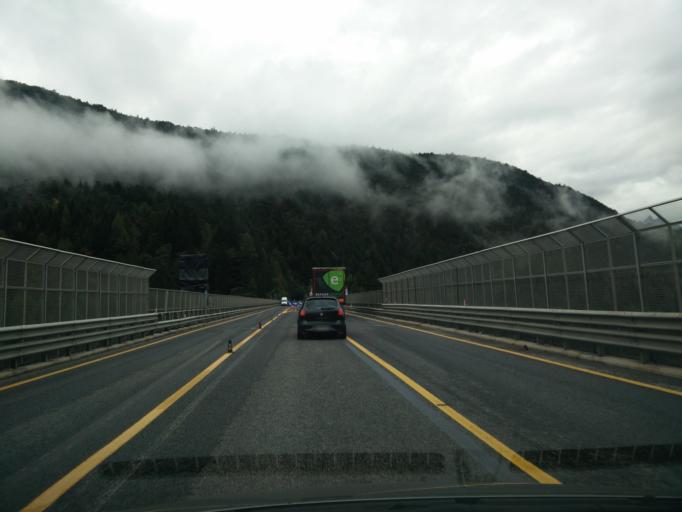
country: IT
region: Veneto
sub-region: Provincia di Belluno
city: Perarolo di Cadore
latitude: 46.4058
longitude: 12.3696
